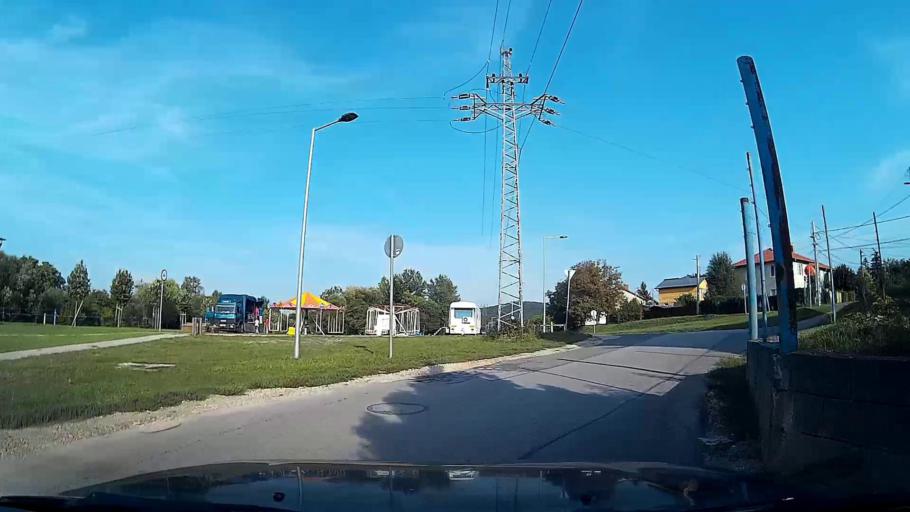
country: HU
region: Pest
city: Budaors
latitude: 47.4400
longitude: 18.9688
